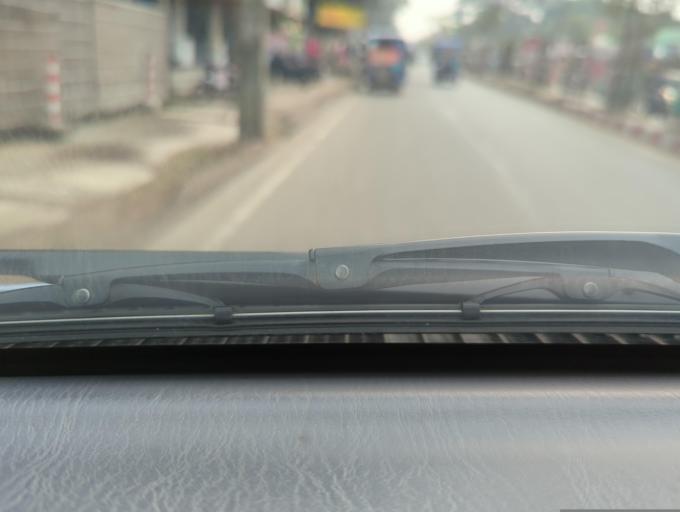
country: BD
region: Sylhet
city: Maulavi Bazar
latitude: 24.4821
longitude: 91.7655
